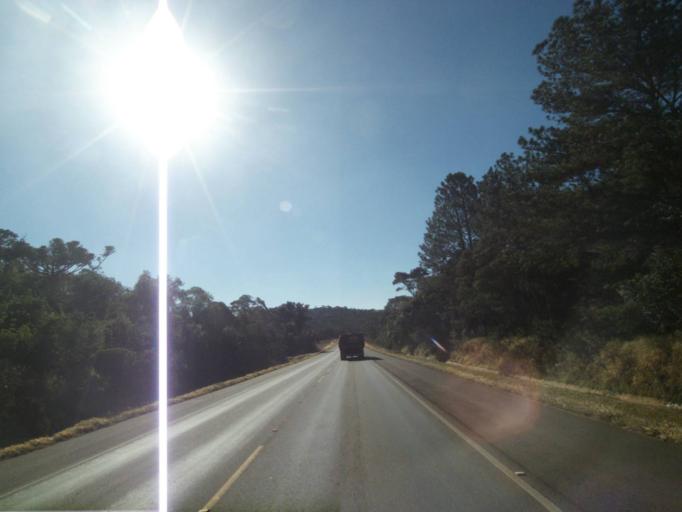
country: BR
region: Parana
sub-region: Tibagi
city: Tibagi
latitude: -24.6582
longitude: -50.4526
